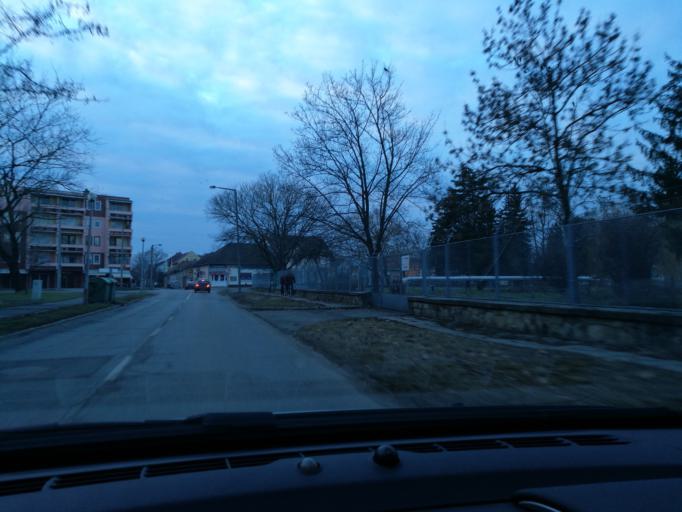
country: HU
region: Szabolcs-Szatmar-Bereg
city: Nyiregyhaza
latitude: 47.9689
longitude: 21.7098
